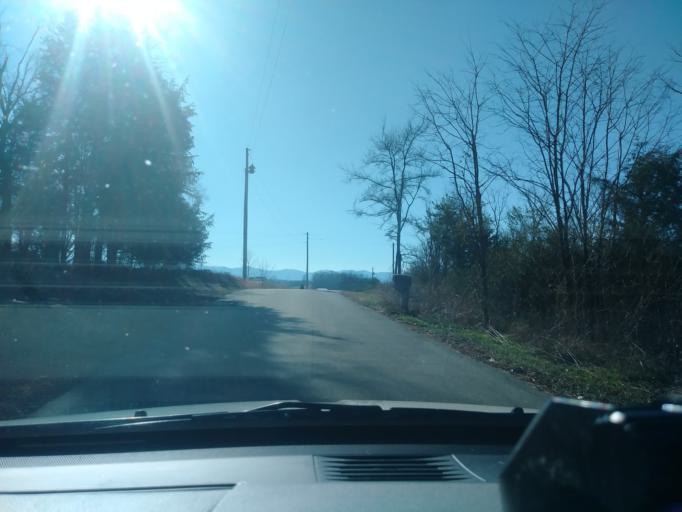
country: US
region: Tennessee
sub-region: Greene County
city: Mosheim
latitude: 36.1019
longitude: -82.9108
